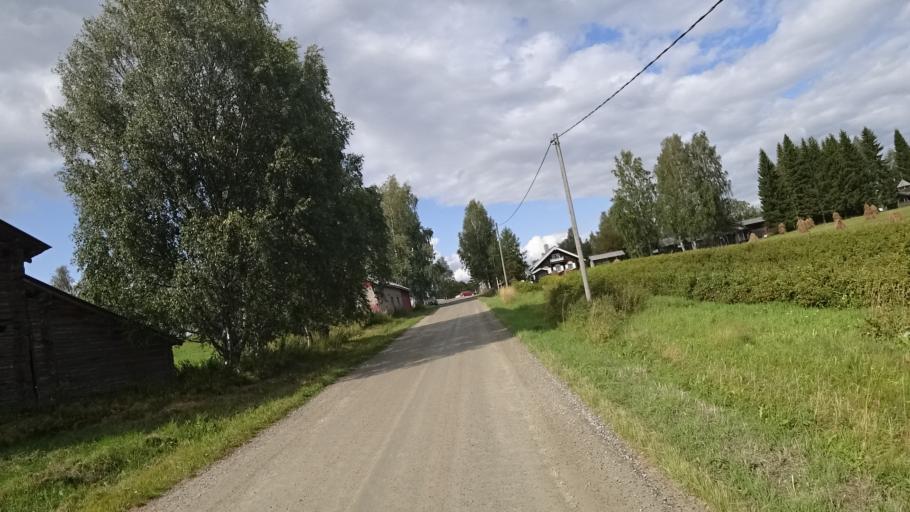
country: FI
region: North Karelia
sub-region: Joensuu
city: Ilomantsi
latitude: 62.6564
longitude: 30.9394
